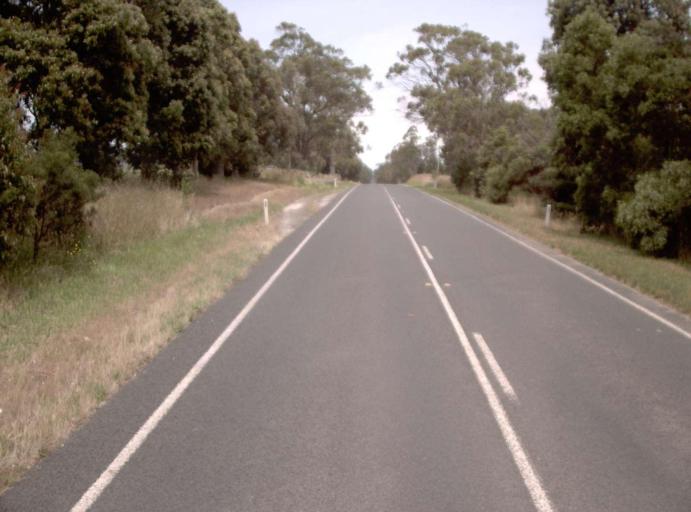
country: AU
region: Victoria
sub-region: Latrobe
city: Traralgon
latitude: -38.5062
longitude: 146.7100
